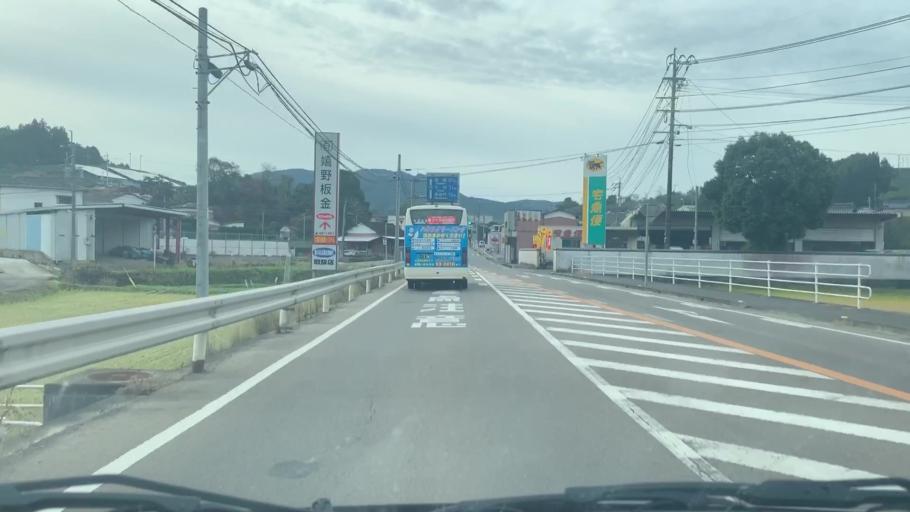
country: JP
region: Saga Prefecture
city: Ureshinomachi-shimojuku
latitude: 33.1158
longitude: 130.0017
